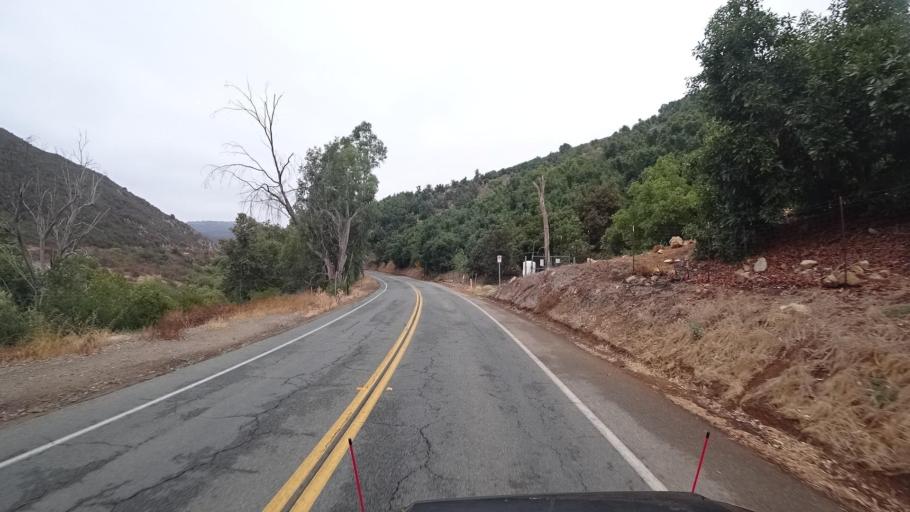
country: US
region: California
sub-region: San Diego County
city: San Marcos
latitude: 33.0853
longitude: -117.1539
